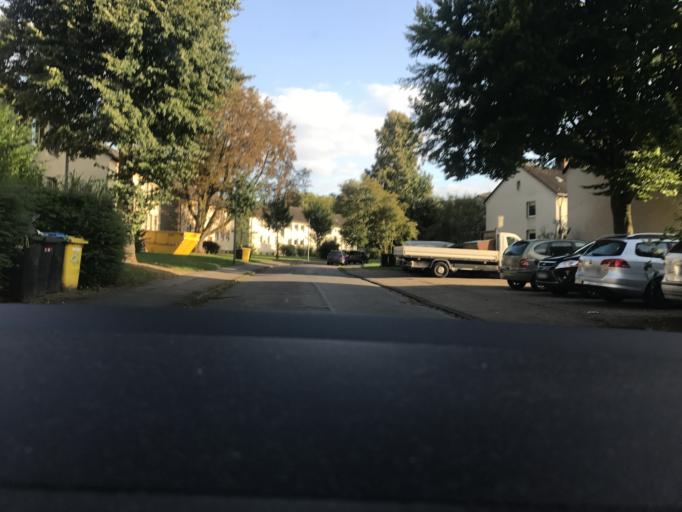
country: DE
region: North Rhine-Westphalia
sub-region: Regierungsbezirk Munster
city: Gelsenkirchen
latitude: 51.5329
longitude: 7.1175
